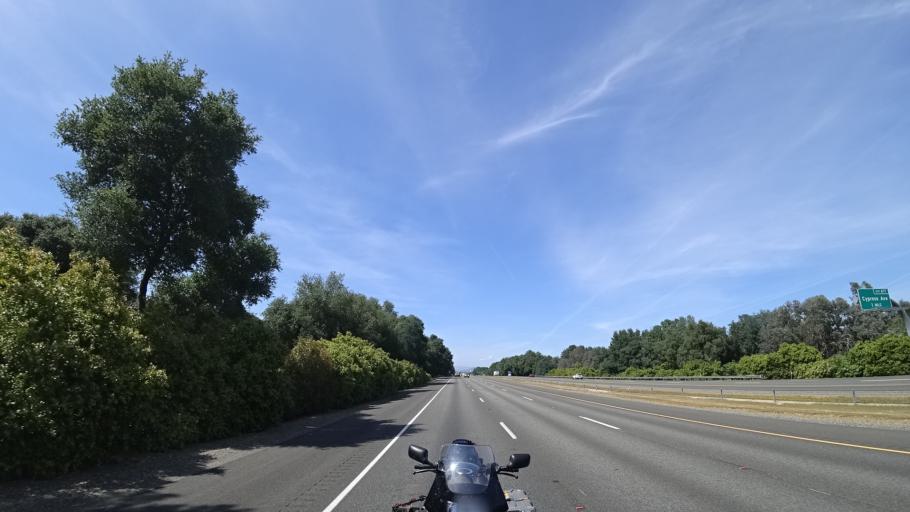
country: US
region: California
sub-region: Shasta County
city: Redding
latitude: 40.5548
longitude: -122.3564
